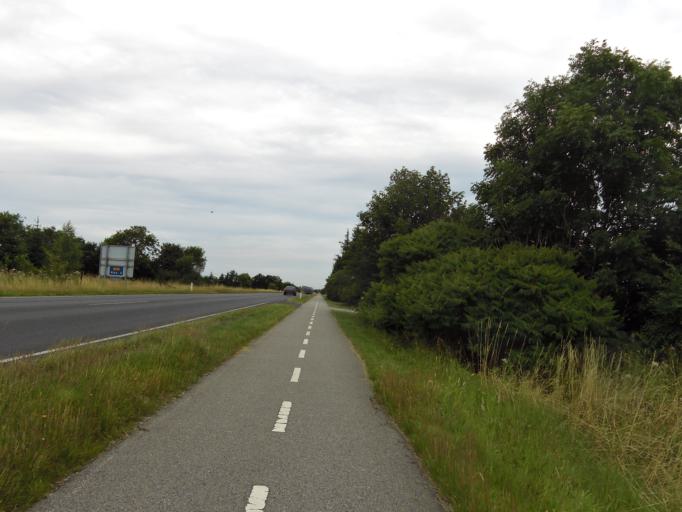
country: DK
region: South Denmark
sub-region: Esbjerg Kommune
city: Ribe
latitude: 55.3150
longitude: 8.7852
